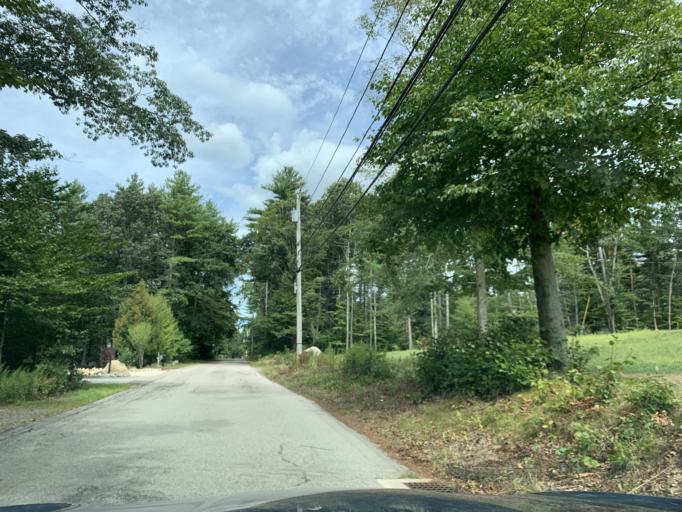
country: US
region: Rhode Island
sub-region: Washington County
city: Exeter
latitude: 41.5415
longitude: -71.6162
